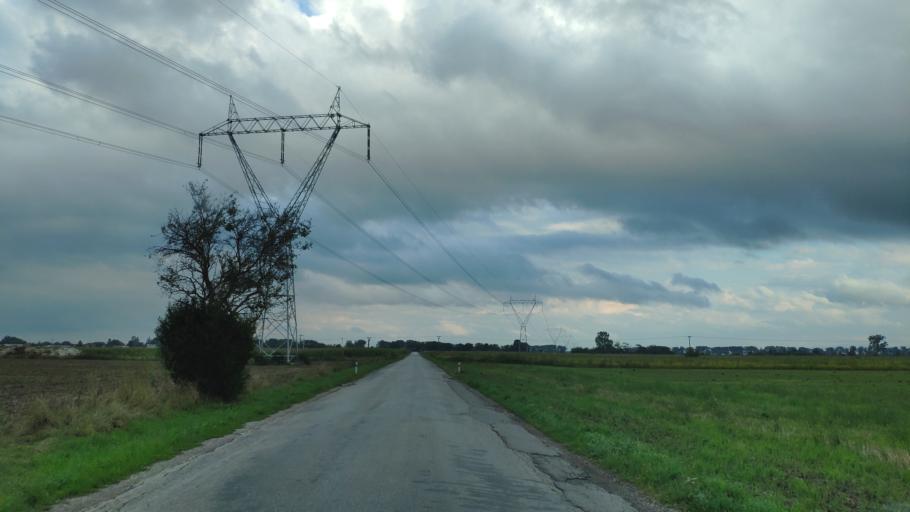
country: SK
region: Kosicky
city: Moldava nad Bodvou
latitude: 48.5838
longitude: 20.9763
